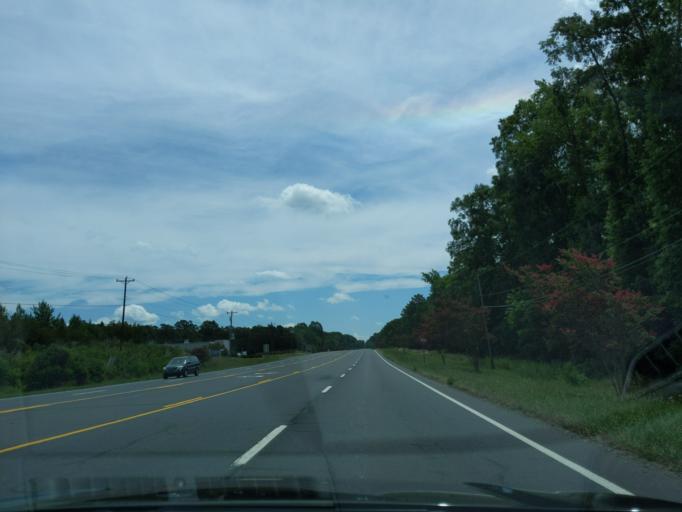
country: US
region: North Carolina
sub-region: Stanly County
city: Albemarle
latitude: 35.4642
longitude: -80.2521
